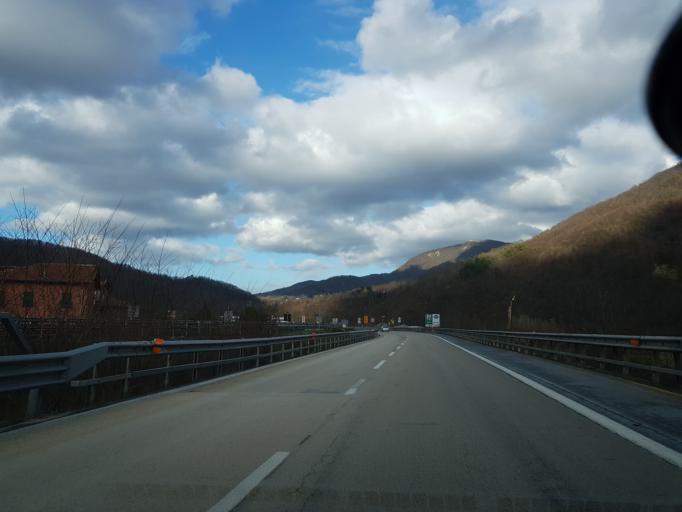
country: IT
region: Liguria
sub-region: Provincia di Genova
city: Ronco Scrivia
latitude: 44.5956
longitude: 8.9544
